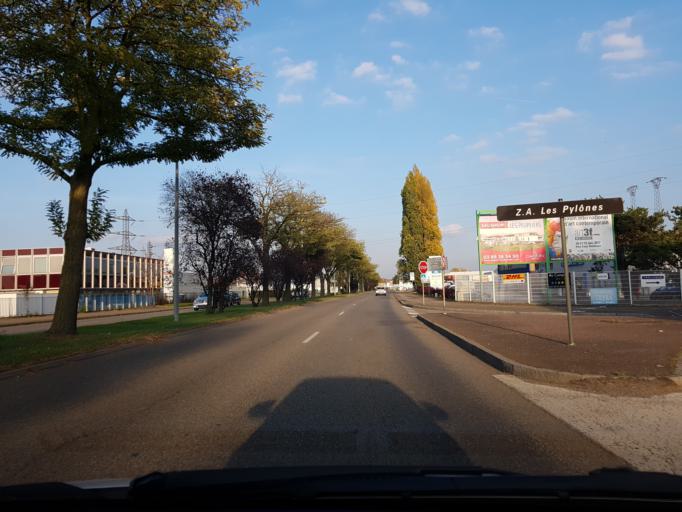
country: FR
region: Alsace
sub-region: Departement du Haut-Rhin
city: Riedisheim
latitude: 47.7664
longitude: 7.3800
